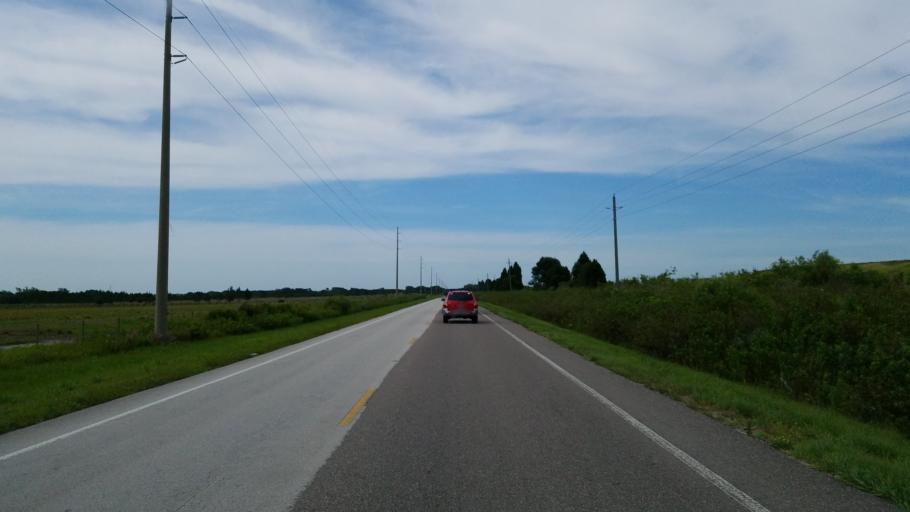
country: US
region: Florida
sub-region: Hillsborough County
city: Balm
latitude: 27.6620
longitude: -82.1462
